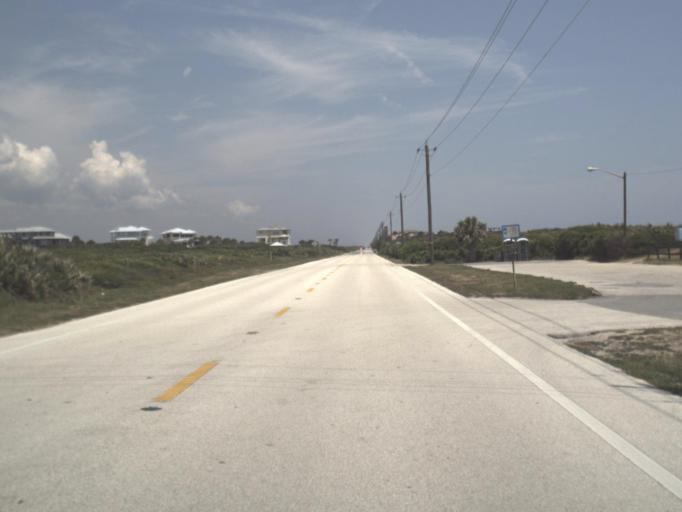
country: US
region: Florida
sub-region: Saint Johns County
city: Villano Beach
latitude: 29.9901
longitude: -81.3152
